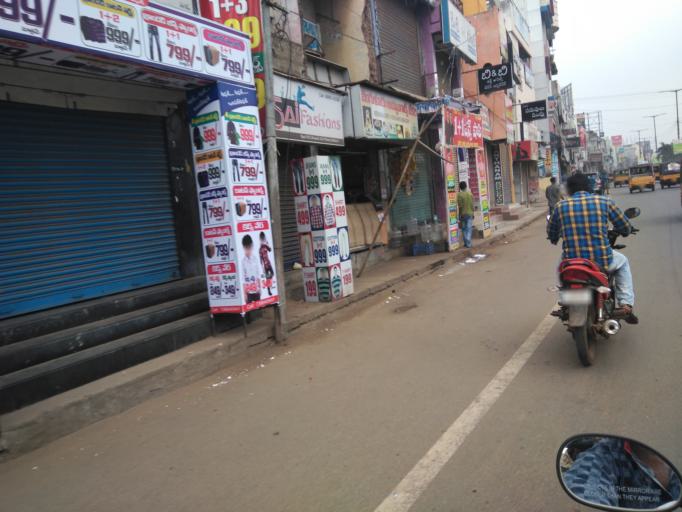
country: IN
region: Andhra Pradesh
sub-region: Nellore
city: Nellore
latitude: 14.4479
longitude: 79.9824
